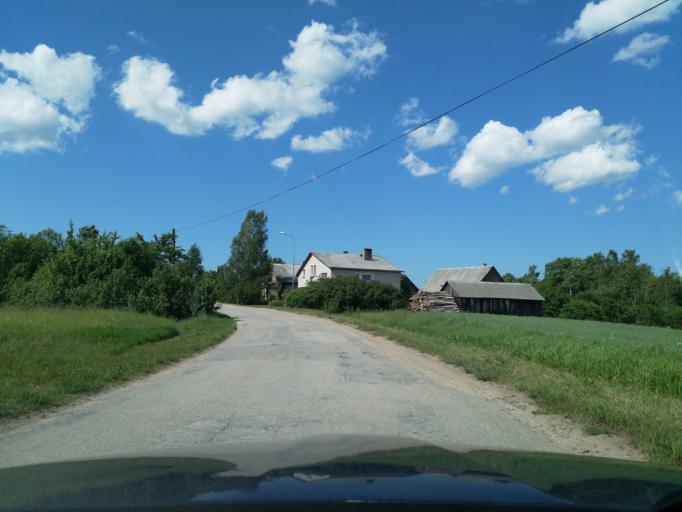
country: LV
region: Alsunga
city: Alsunga
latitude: 56.9725
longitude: 21.5684
